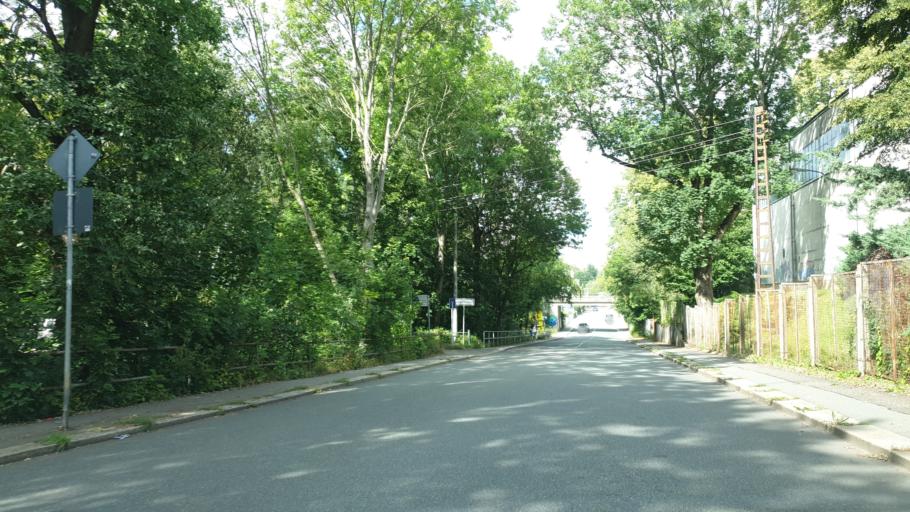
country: DE
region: Saxony
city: Neukirchen
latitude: 50.8161
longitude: 12.8708
